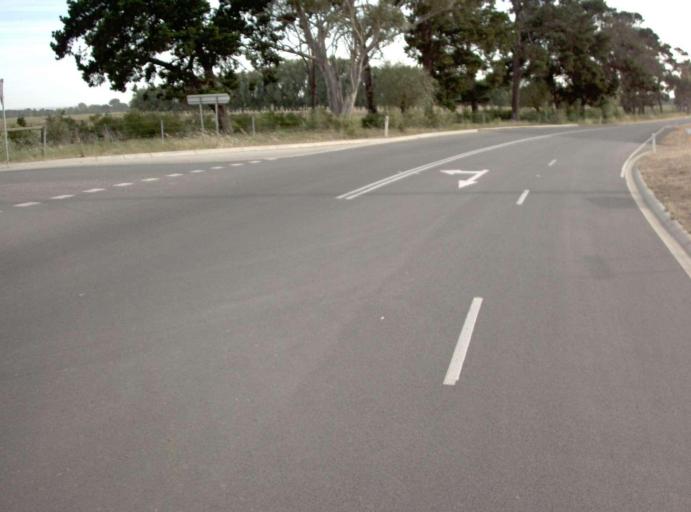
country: AU
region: Victoria
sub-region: Wellington
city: Heyfield
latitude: -38.0086
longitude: 146.7795
